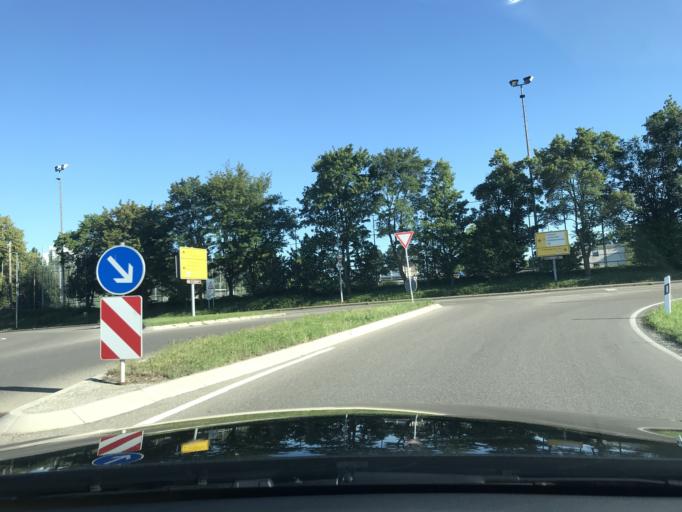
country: DE
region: Baden-Wuerttemberg
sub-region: Regierungsbezirk Stuttgart
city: Stuttgart Muehlhausen
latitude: 48.8333
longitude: 9.2517
